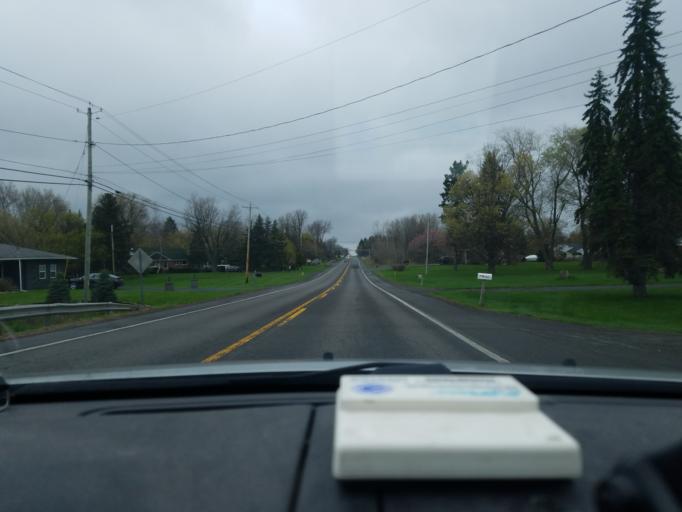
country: US
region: New York
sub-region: Onondaga County
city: North Syracuse
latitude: 43.1509
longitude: -76.1087
